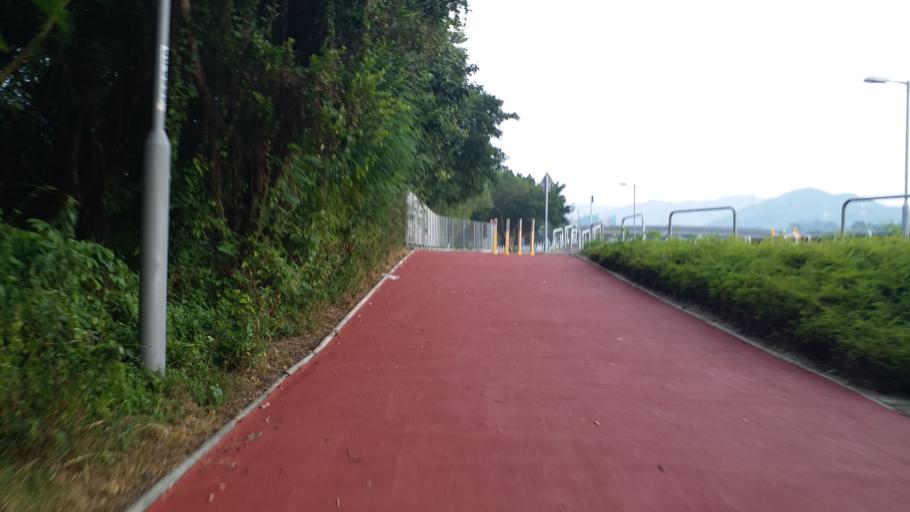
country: HK
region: Yuen Long
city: Yuen Long Kau Hui
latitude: 22.4562
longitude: 114.0483
